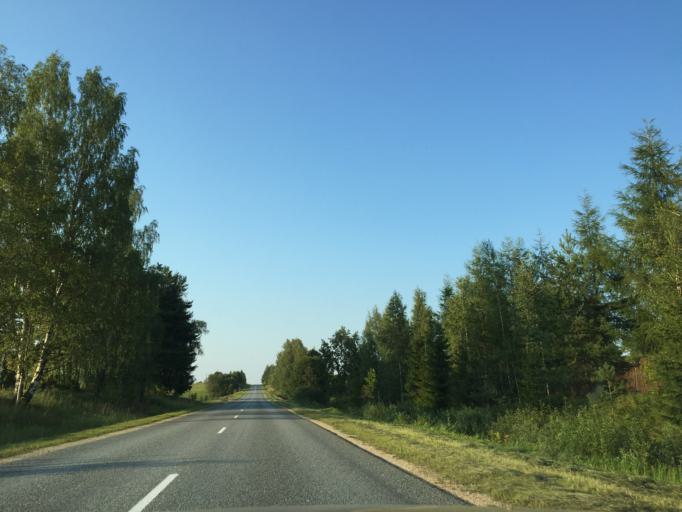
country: LV
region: Limbazu Rajons
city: Limbazi
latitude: 57.5659
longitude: 24.7676
